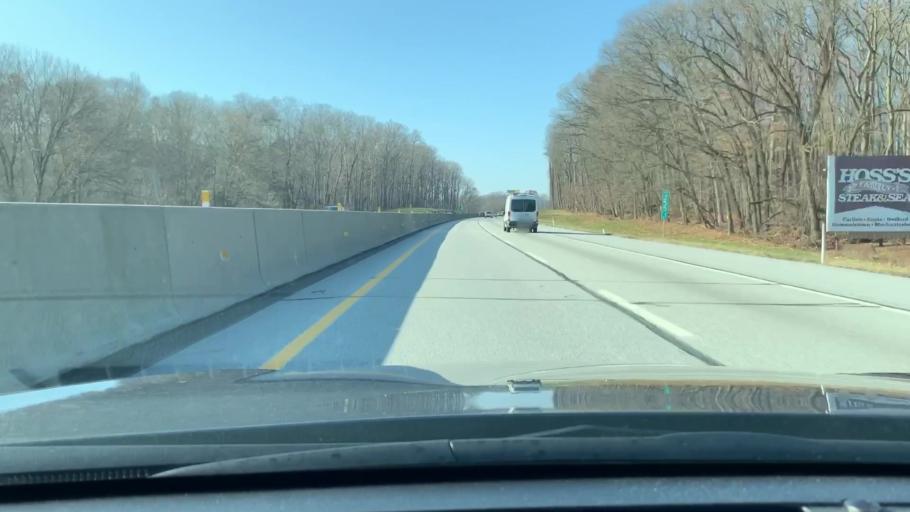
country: US
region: Pennsylvania
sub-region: Lancaster County
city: Elizabethtown
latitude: 40.2071
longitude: -76.6431
